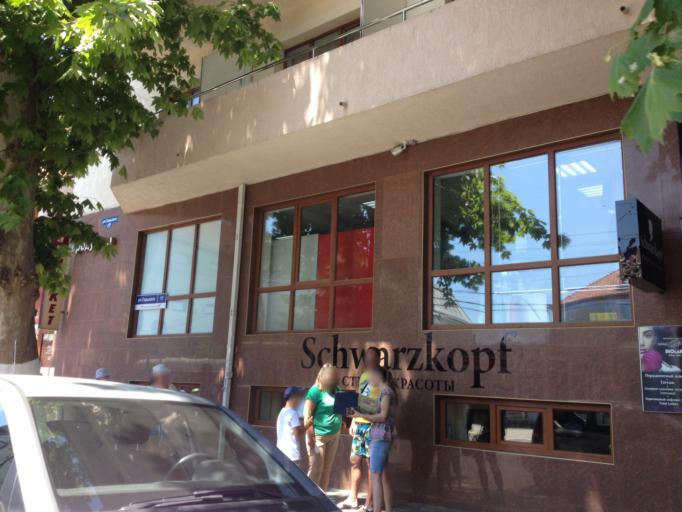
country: RU
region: Krasnodarskiy
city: Anapa
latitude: 44.8984
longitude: 37.3216
